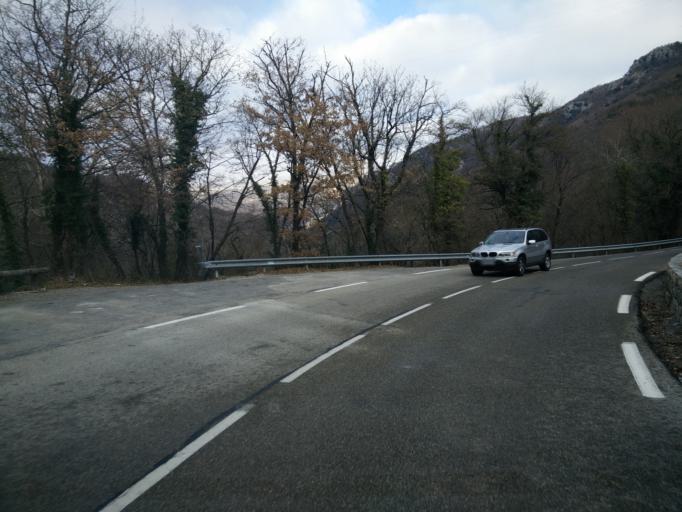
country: FR
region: Provence-Alpes-Cote d'Azur
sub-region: Departement des Alpes-Maritimes
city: Tourrettes-sur-Loup
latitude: 43.7629
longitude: 6.9876
